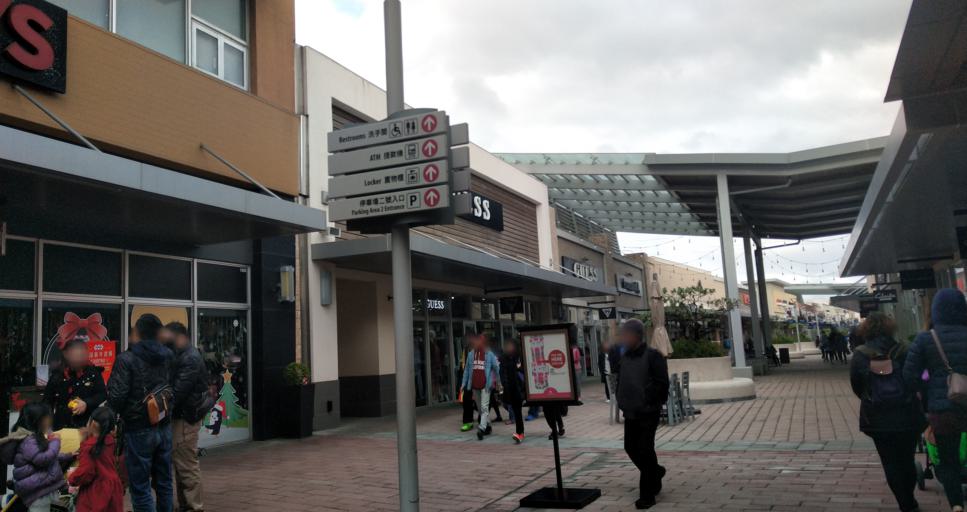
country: TW
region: Taiwan
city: Taoyuan City
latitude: 25.0147
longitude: 121.2132
